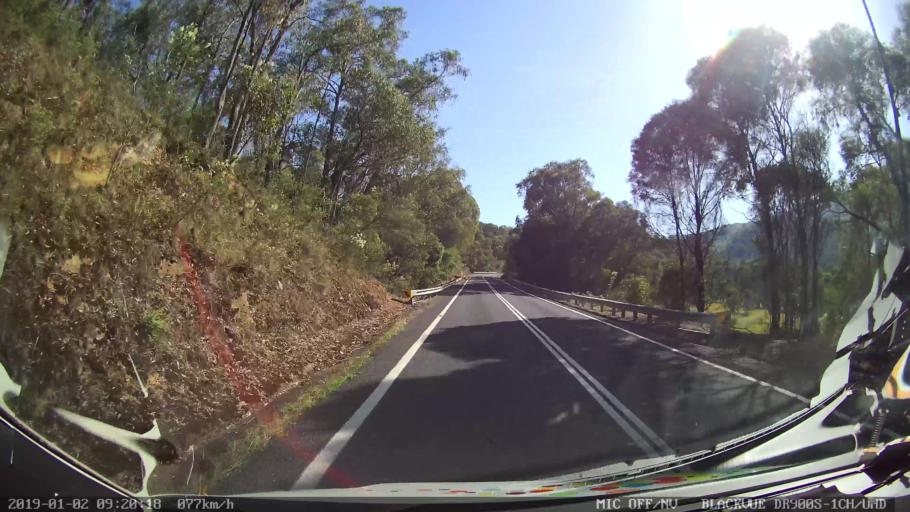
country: AU
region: New South Wales
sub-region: Tumut Shire
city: Tumut
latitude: -35.4134
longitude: 148.2823
